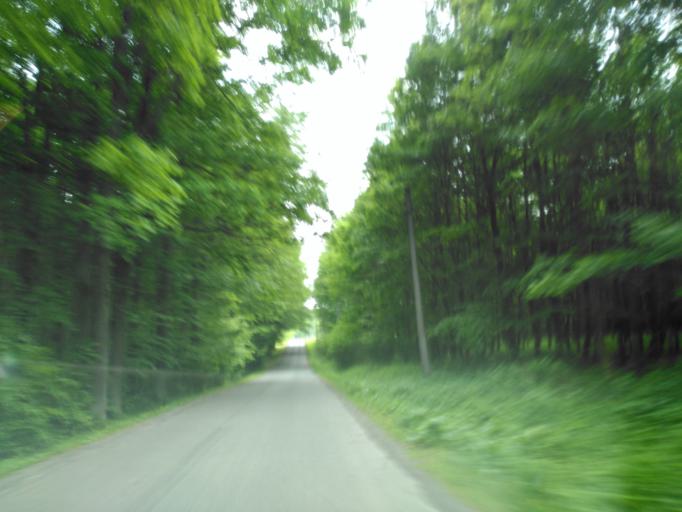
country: CZ
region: Plzensky
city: Zbiroh
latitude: 49.9209
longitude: 13.8266
